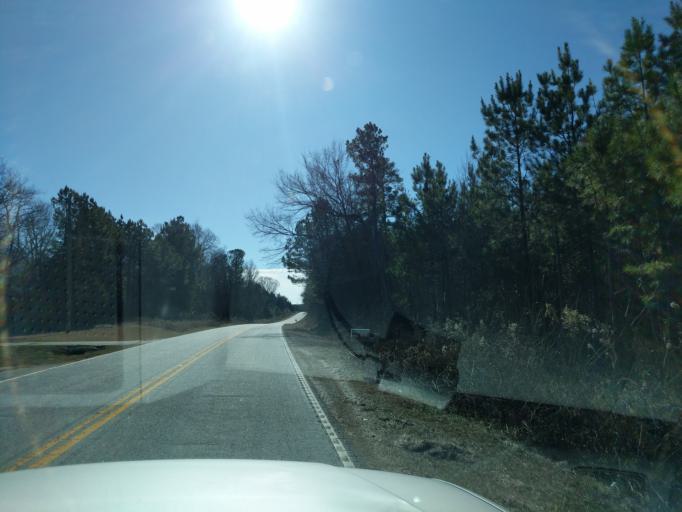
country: US
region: South Carolina
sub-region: Laurens County
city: Joanna
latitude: 34.3504
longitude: -81.8569
